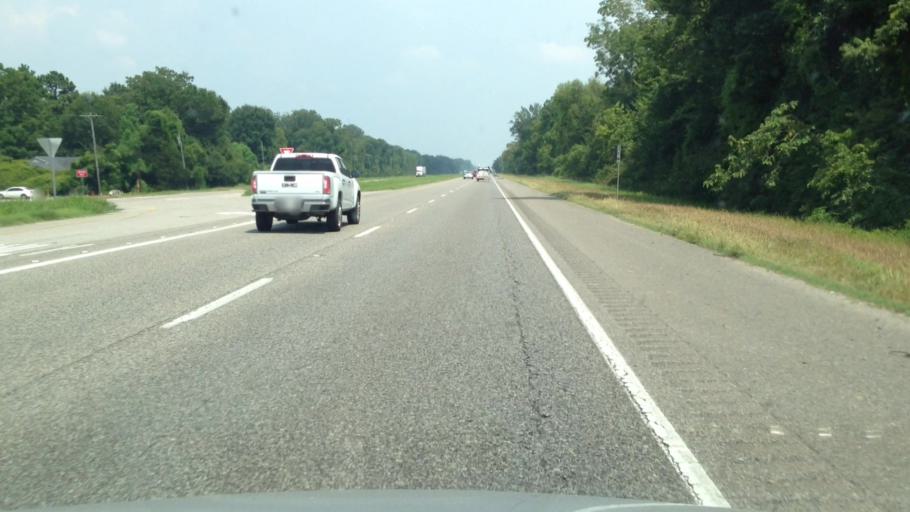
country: US
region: Louisiana
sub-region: West Baton Rouge Parish
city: Erwinville
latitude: 30.5126
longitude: -91.3471
